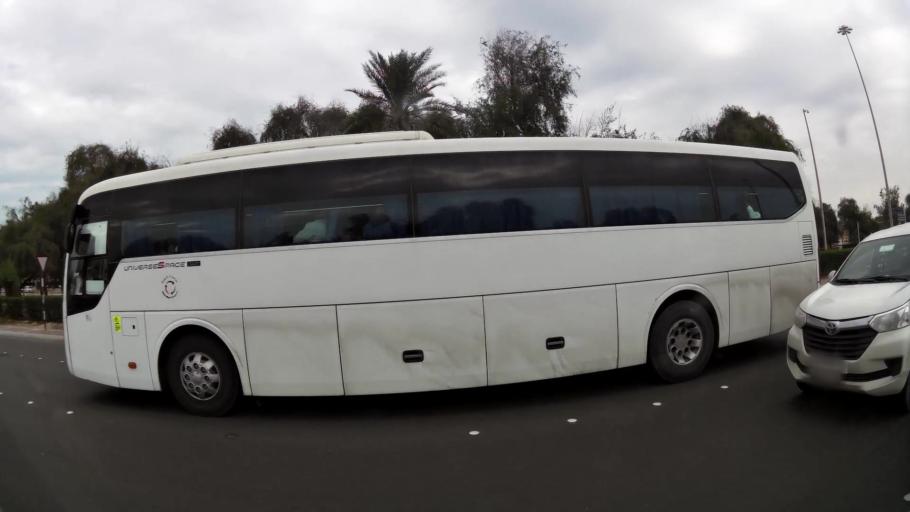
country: AE
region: Abu Dhabi
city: Abu Dhabi
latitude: 24.4366
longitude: 54.4041
